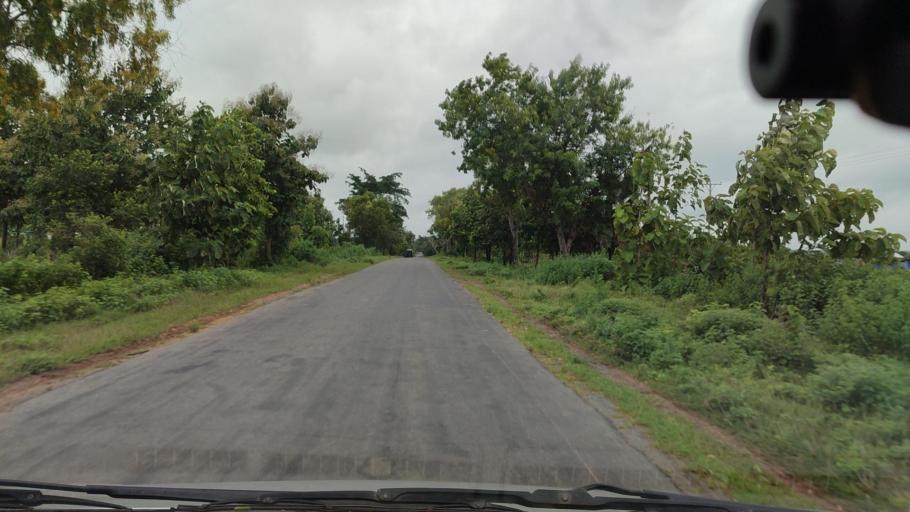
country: MM
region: Bago
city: Pyay
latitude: 18.8867
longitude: 95.4669
